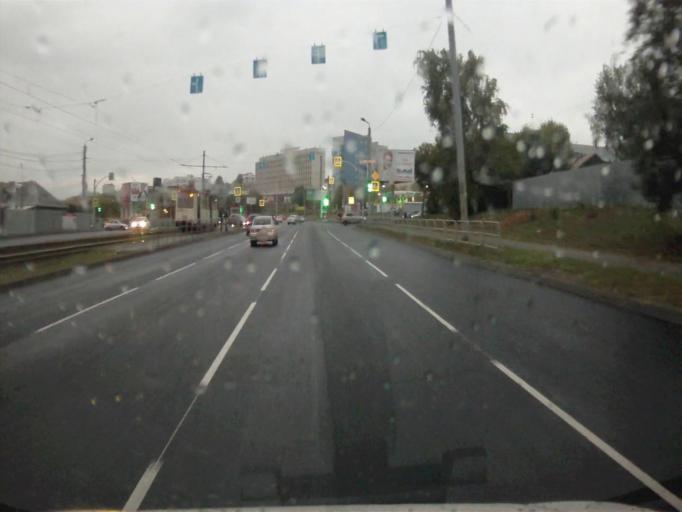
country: RU
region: Chelyabinsk
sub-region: Gorod Chelyabinsk
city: Chelyabinsk
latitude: 55.1876
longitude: 61.3619
